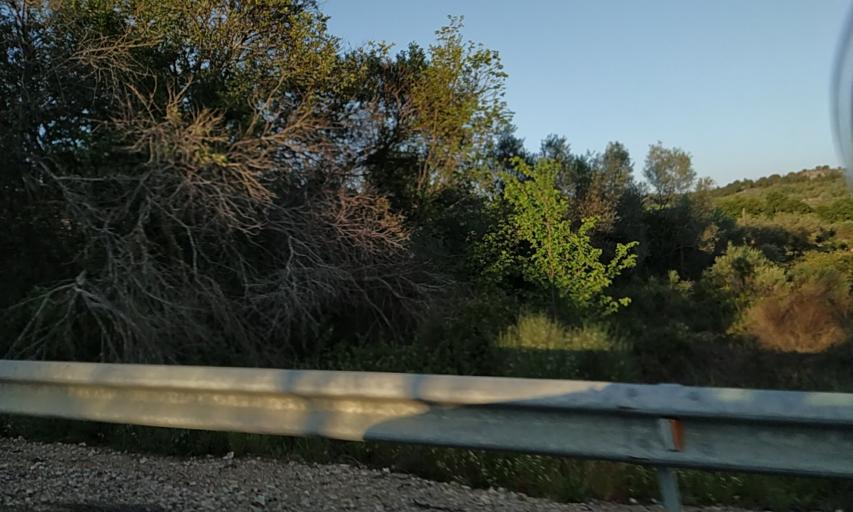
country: ES
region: Extremadura
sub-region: Provincia de Caceres
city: Valencia de Alcantara
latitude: 39.4002
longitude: -7.2509
